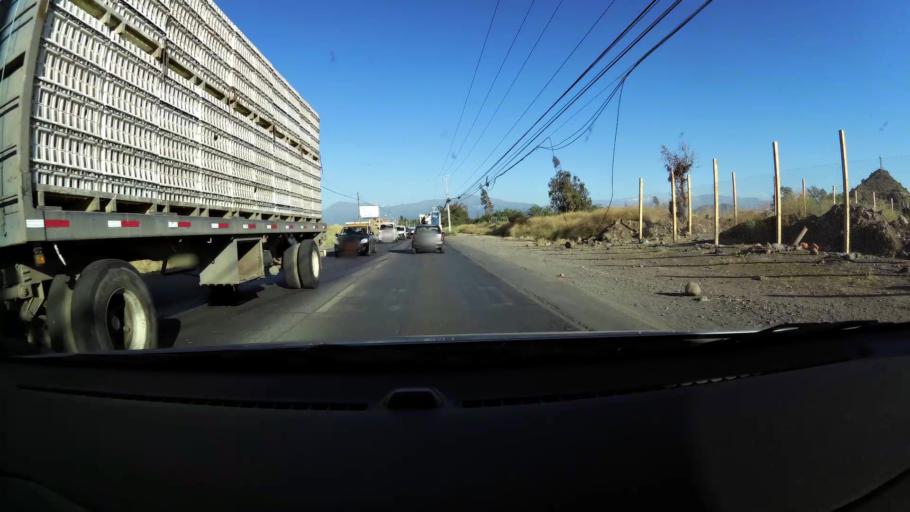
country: CL
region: Santiago Metropolitan
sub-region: Provincia de Maipo
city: San Bernardo
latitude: -33.6059
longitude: -70.6780
